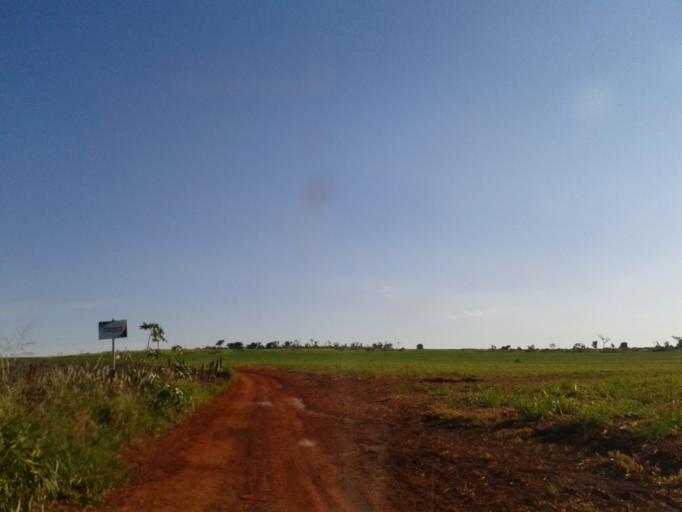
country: BR
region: Minas Gerais
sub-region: Centralina
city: Centralina
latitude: -18.6750
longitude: -49.2727
